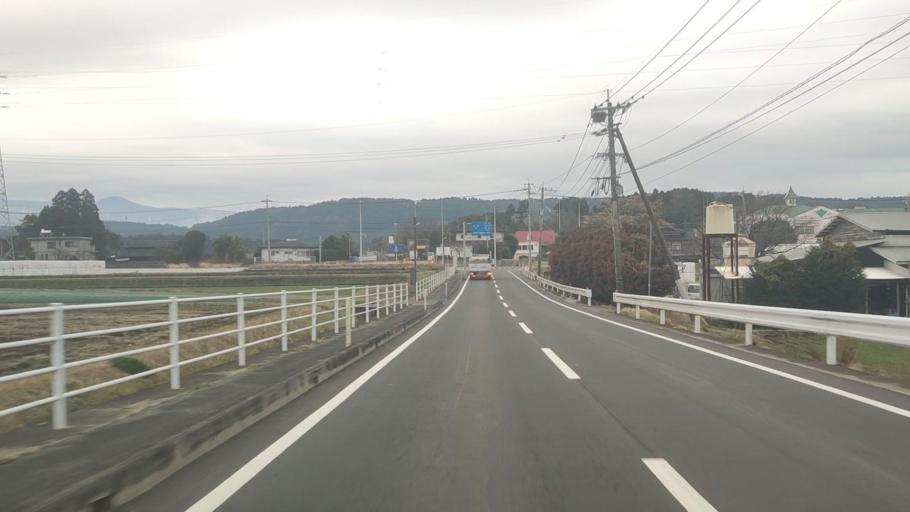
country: JP
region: Kumamoto
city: Ozu
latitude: 32.8665
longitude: 130.8906
